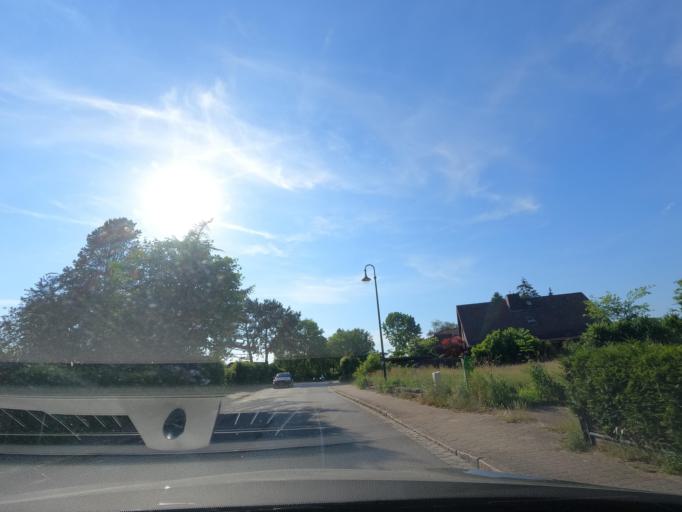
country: DE
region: Schleswig-Holstein
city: Gross Nordende
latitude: 53.6946
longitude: 9.6519
